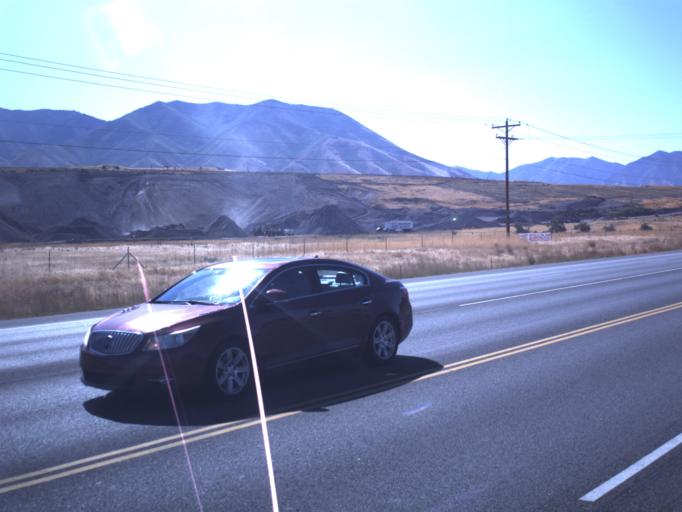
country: US
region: Utah
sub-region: Tooele County
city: Stansbury park
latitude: 40.6466
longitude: -112.2884
